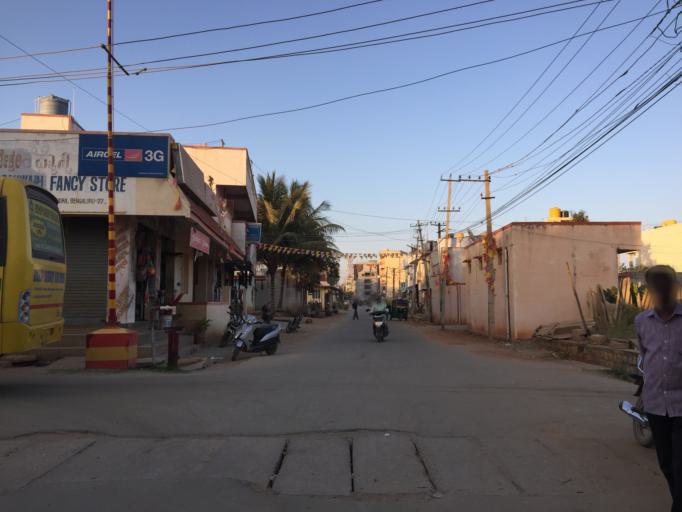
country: IN
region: Karnataka
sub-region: Bangalore Urban
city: Yelahanka
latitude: 13.0530
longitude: 77.6283
